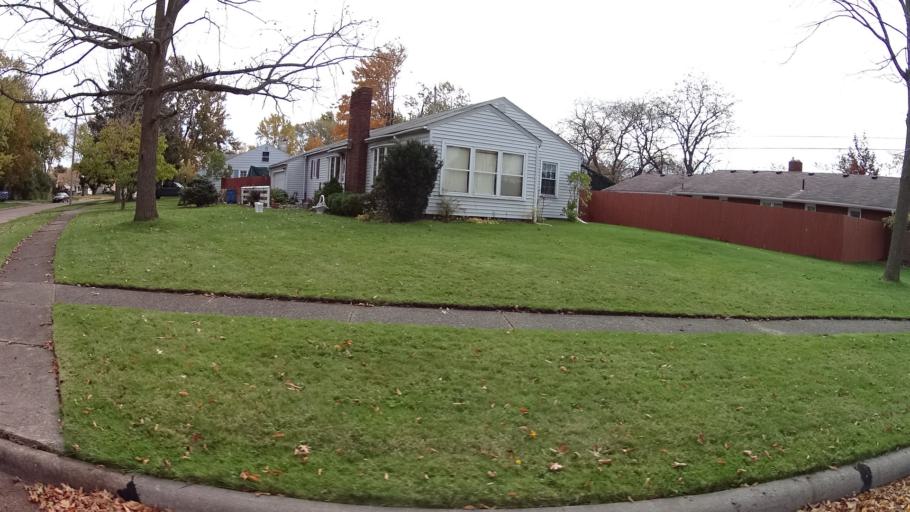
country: US
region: Ohio
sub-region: Lorain County
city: Lorain
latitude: 41.4765
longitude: -82.1509
